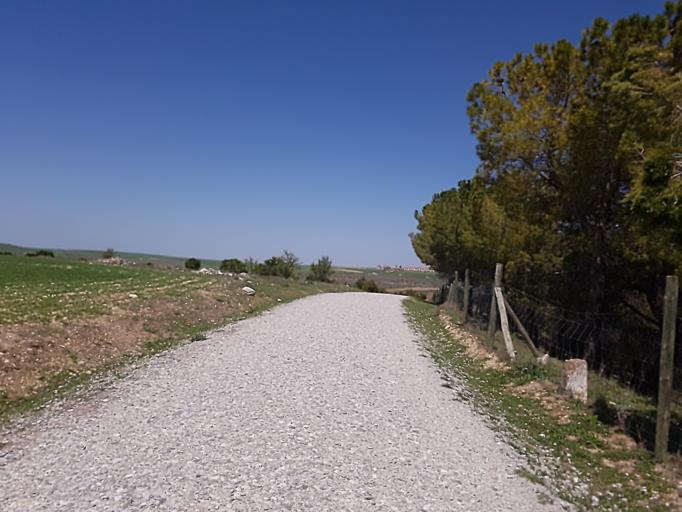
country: ES
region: Castille and Leon
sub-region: Provincia de Segovia
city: Segovia
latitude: 40.9504
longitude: -4.1345
